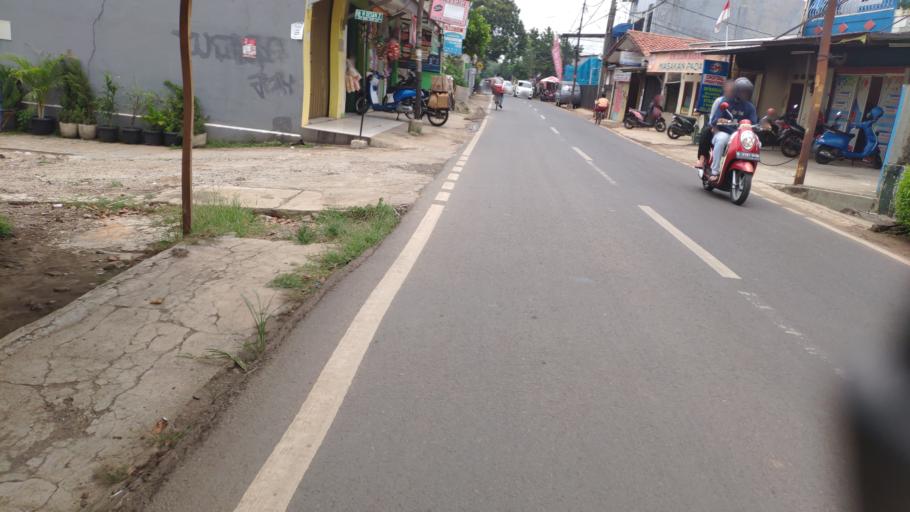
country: ID
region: West Java
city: Depok
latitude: -6.3478
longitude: 106.8205
